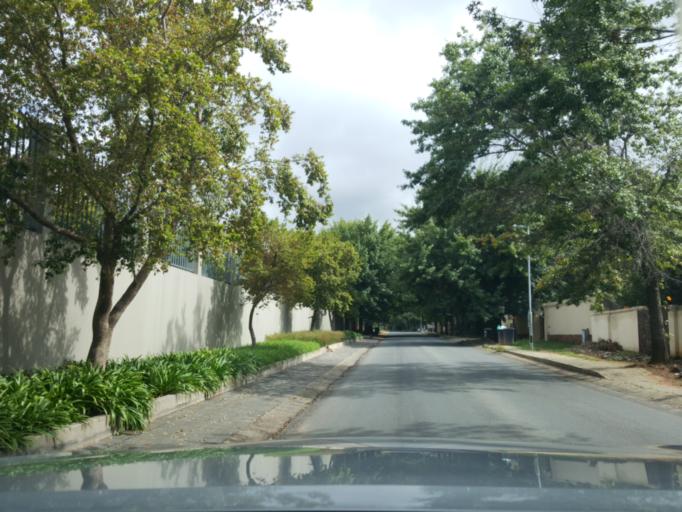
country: ZA
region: Gauteng
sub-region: City of Johannesburg Metropolitan Municipality
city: Johannesburg
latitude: -26.1106
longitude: 27.9988
